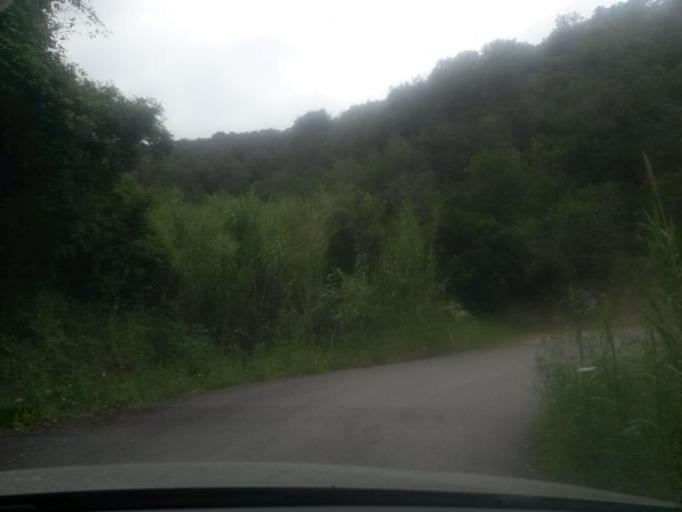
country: IT
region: Tuscany
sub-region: Provincia di Livorno
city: Porto Azzurro
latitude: 42.7439
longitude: 10.4048
